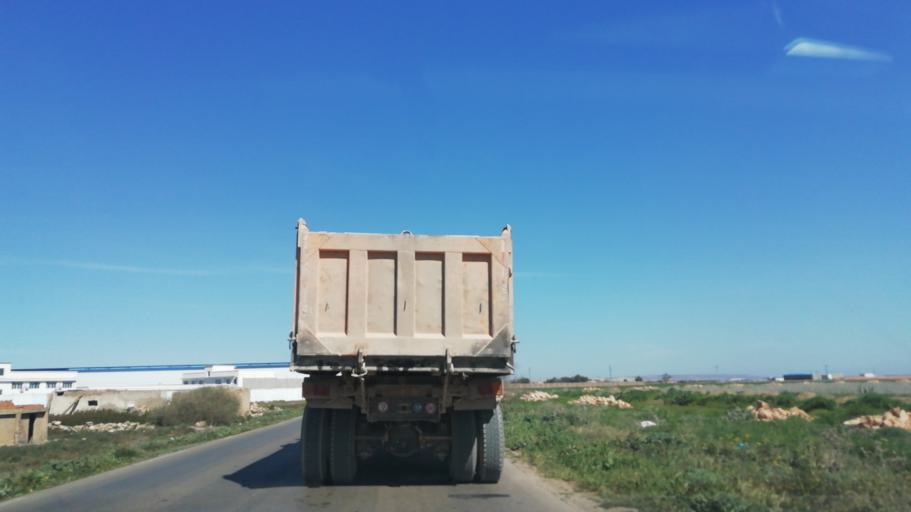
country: DZ
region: Oran
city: Es Senia
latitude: 35.5078
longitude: -0.5921
